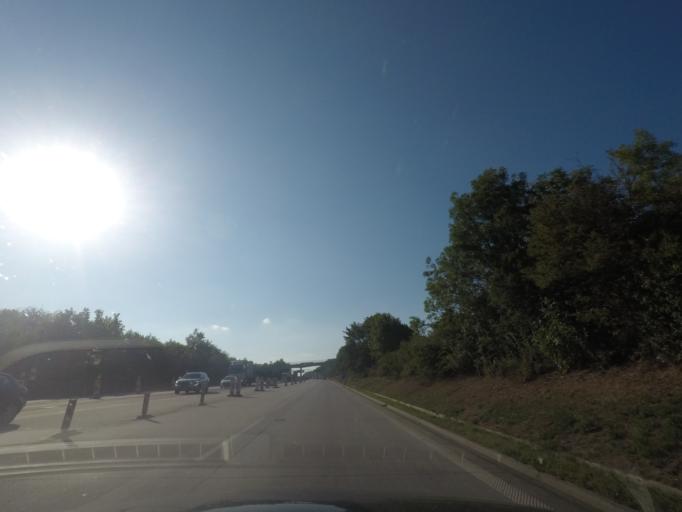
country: CZ
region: Olomoucky
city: Dolni Ujezd
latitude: 49.5540
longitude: 17.5277
